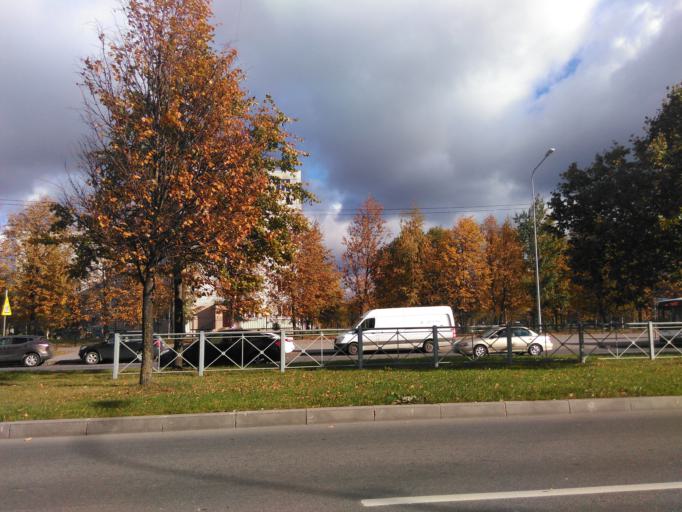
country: RU
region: St.-Petersburg
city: Krasnogvargeisky
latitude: 59.9248
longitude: 30.4888
